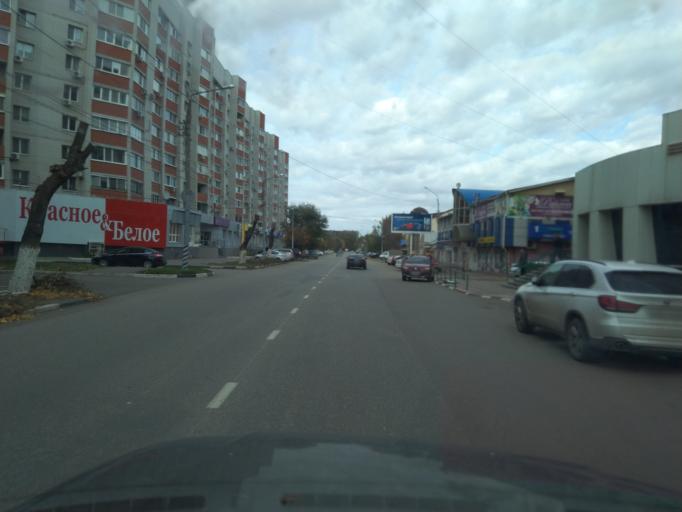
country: RU
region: Saratov
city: Engel's
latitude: 51.4902
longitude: 46.1227
